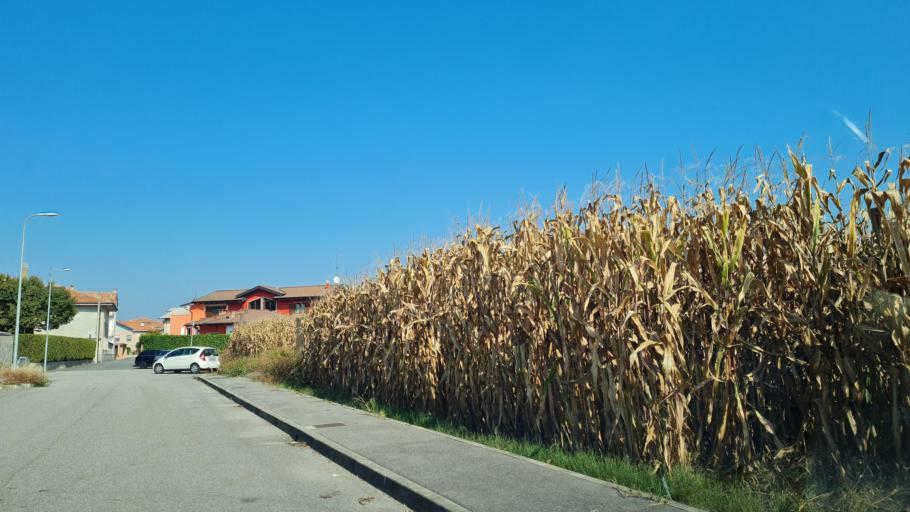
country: IT
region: Piedmont
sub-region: Provincia di Novara
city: Carpignano Sesia
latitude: 45.5304
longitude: 8.4179
